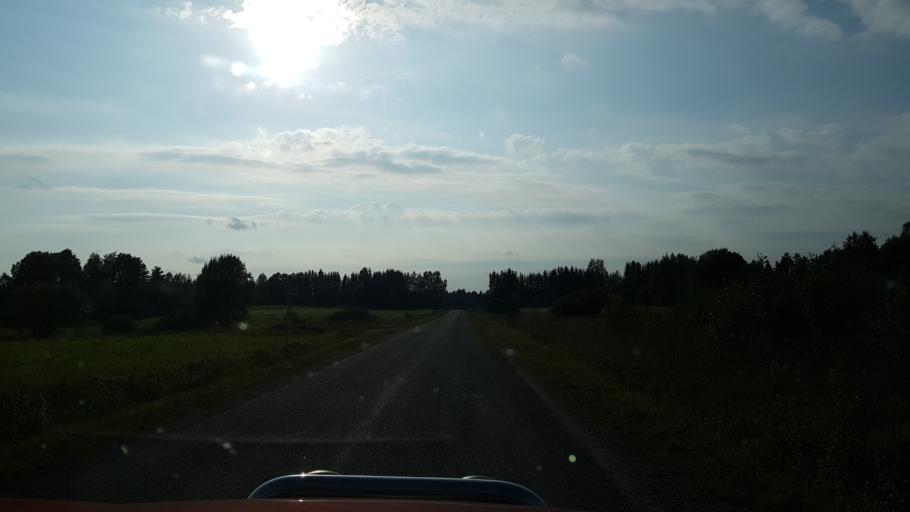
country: EE
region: Polvamaa
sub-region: Polva linn
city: Polva
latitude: 58.1250
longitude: 26.9298
